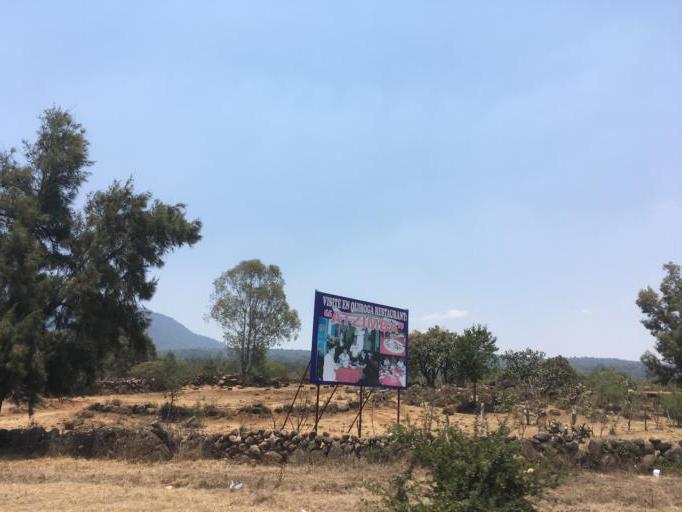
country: MX
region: Michoacan
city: Quiroga
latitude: 19.6518
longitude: -101.4932
